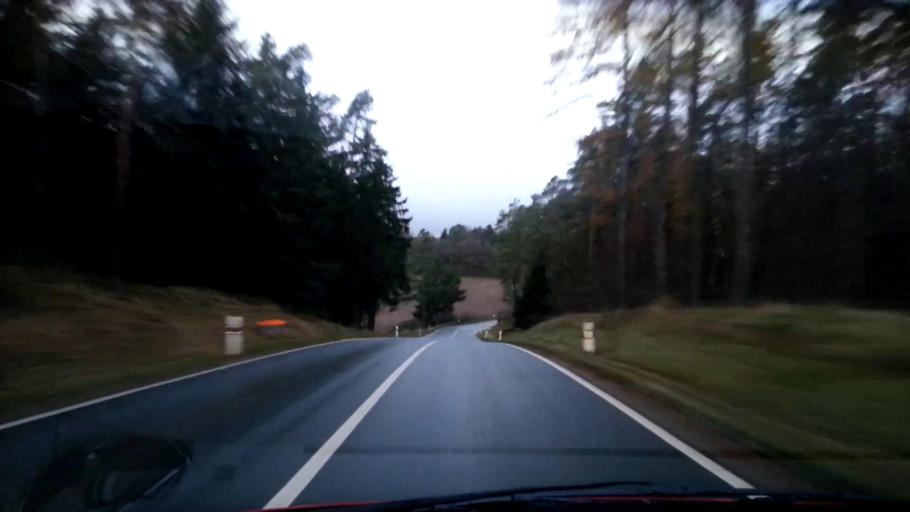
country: DE
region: Bavaria
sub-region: Upper Franconia
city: Konigsfeld
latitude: 49.9433
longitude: 11.1845
